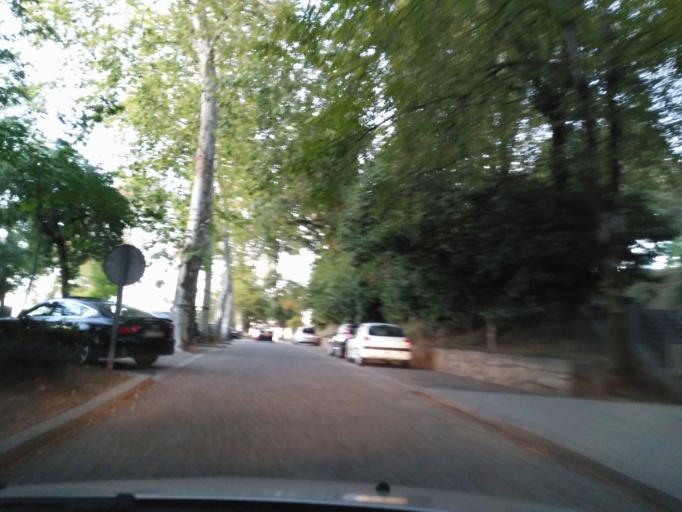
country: PT
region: Braga
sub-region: Braga
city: Adaufe
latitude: 41.5557
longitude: -8.3773
